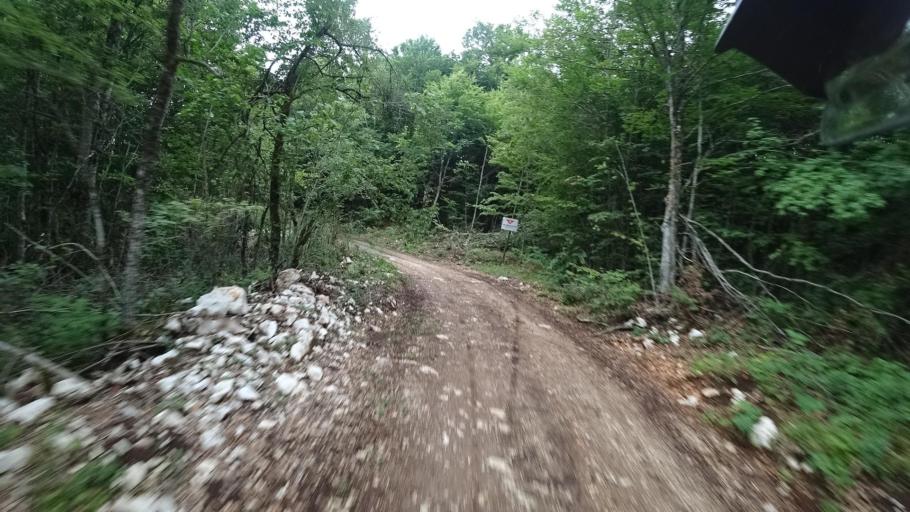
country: HR
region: Licko-Senjska
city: Jezerce
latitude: 44.7715
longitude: 15.4836
